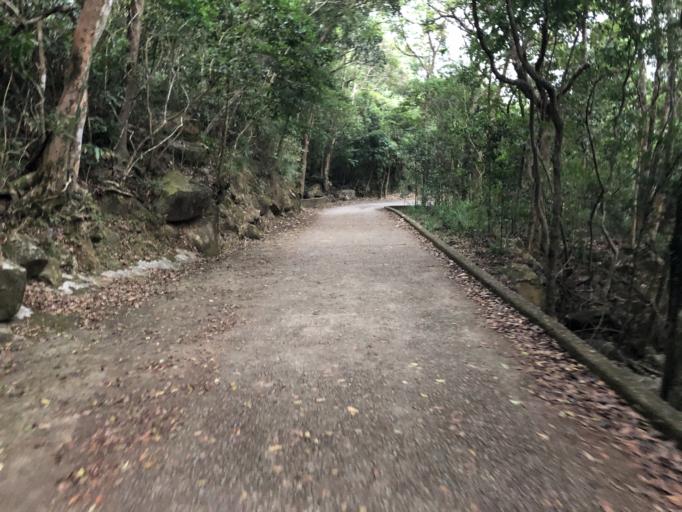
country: HK
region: Wanchai
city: Wan Chai
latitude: 22.2650
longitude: 114.2147
